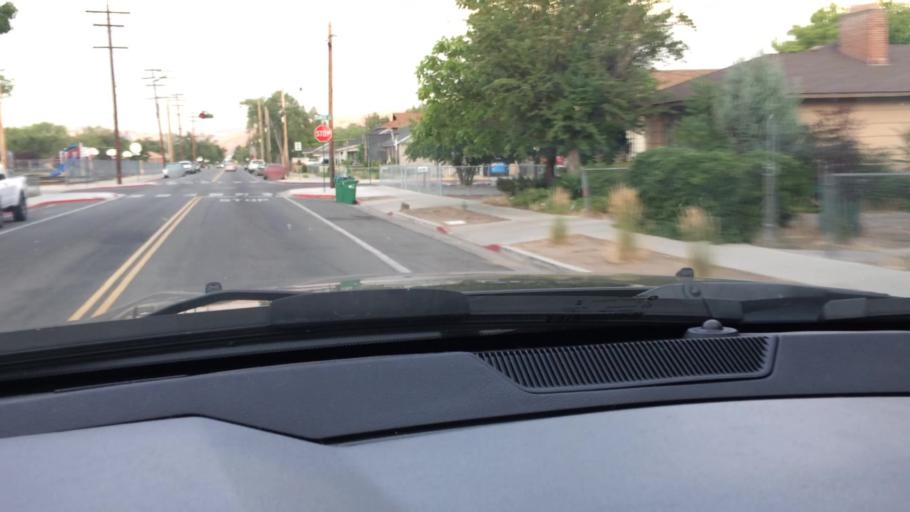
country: US
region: Nevada
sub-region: Washoe County
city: Reno
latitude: 39.5129
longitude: -119.8012
